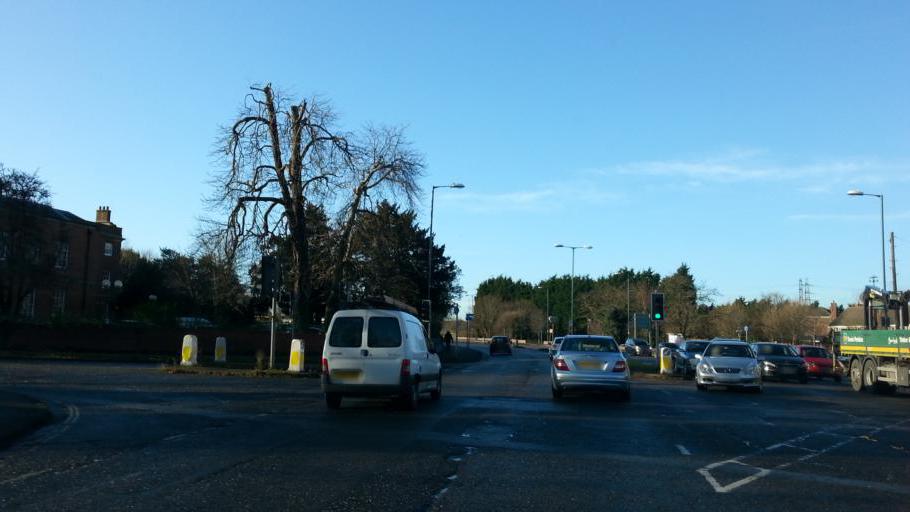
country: GB
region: England
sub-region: Nottingham
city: Nottingham
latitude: 52.9257
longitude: -1.1599
